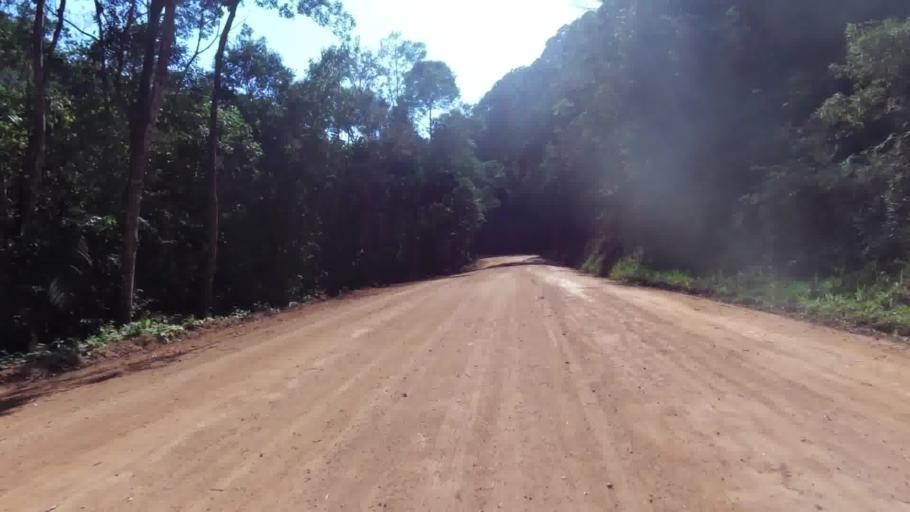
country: BR
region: Espirito Santo
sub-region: Alfredo Chaves
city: Alfredo Chaves
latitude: -20.5400
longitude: -40.8359
